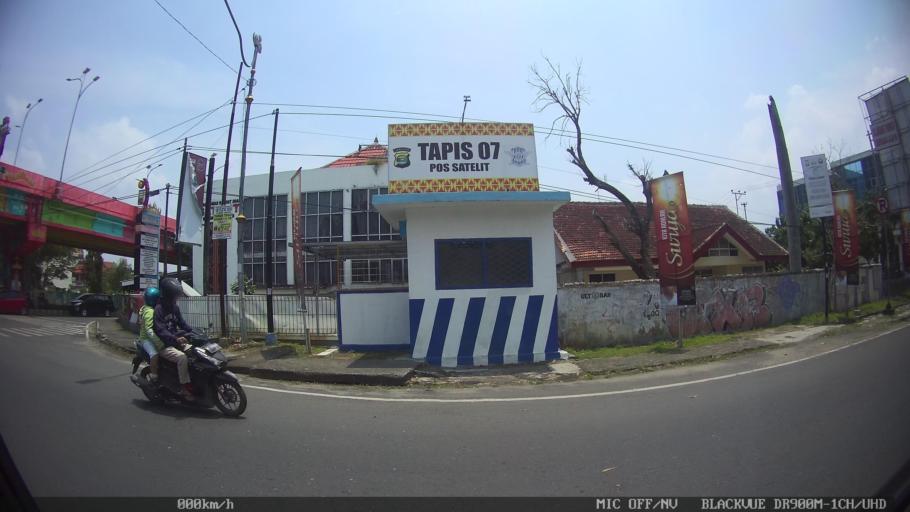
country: ID
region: Lampung
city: Bandarlampung
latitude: -5.4228
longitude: 105.2698
